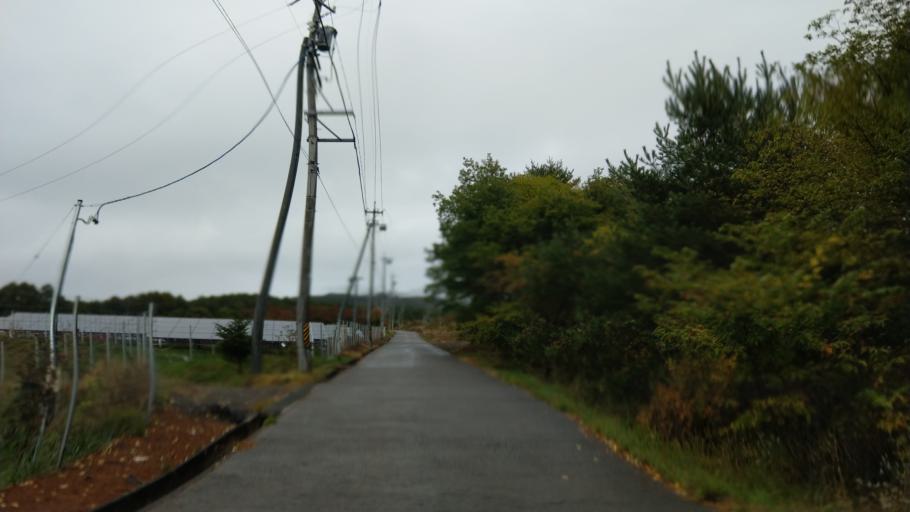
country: JP
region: Nagano
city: Komoro
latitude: 36.3591
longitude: 138.4250
